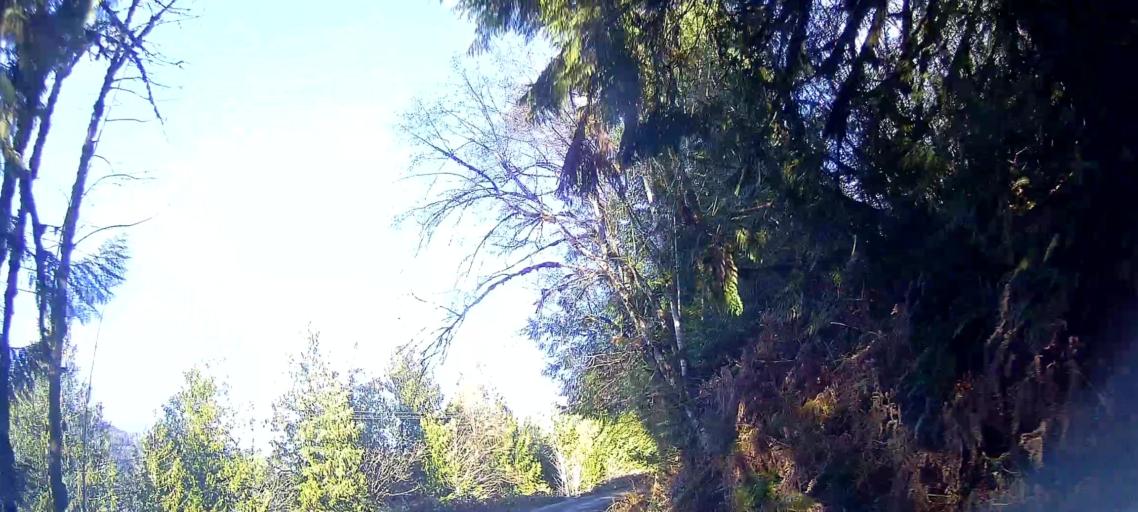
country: US
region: Washington
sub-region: Snohomish County
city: Darrington
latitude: 48.5564
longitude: -121.7263
